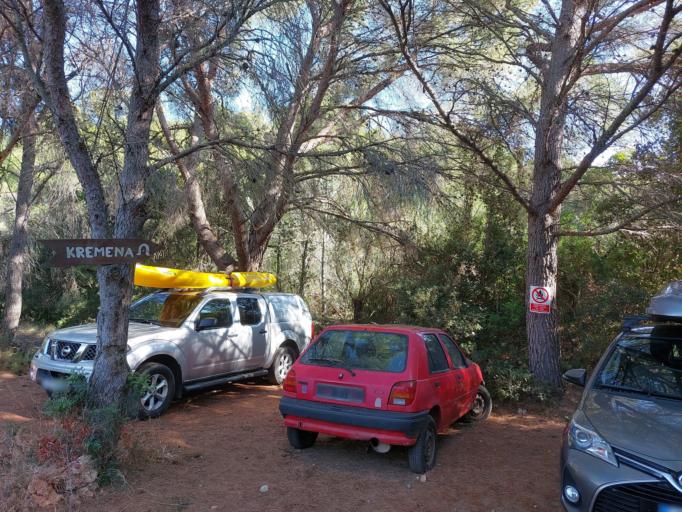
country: HR
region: Dubrovacko-Neretvanska
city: Smokvica
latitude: 42.7632
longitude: 16.8085
